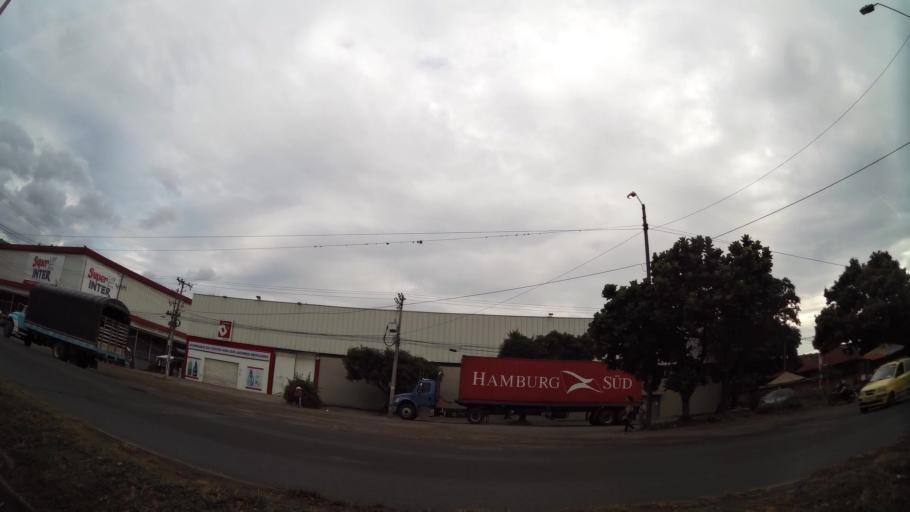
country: CO
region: Valle del Cauca
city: Cali
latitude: 3.4930
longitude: -76.5179
